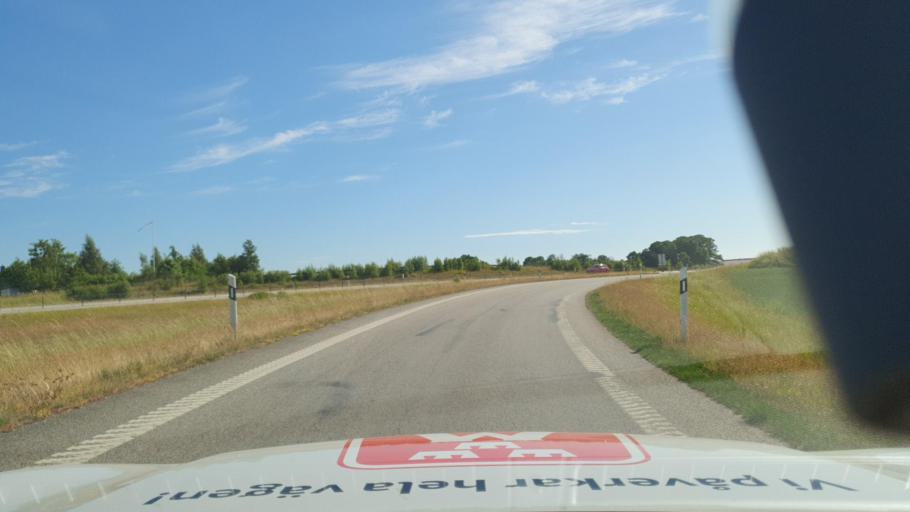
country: SE
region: Skane
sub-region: Skurups Kommun
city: Skurup
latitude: 55.4930
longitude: 13.4789
